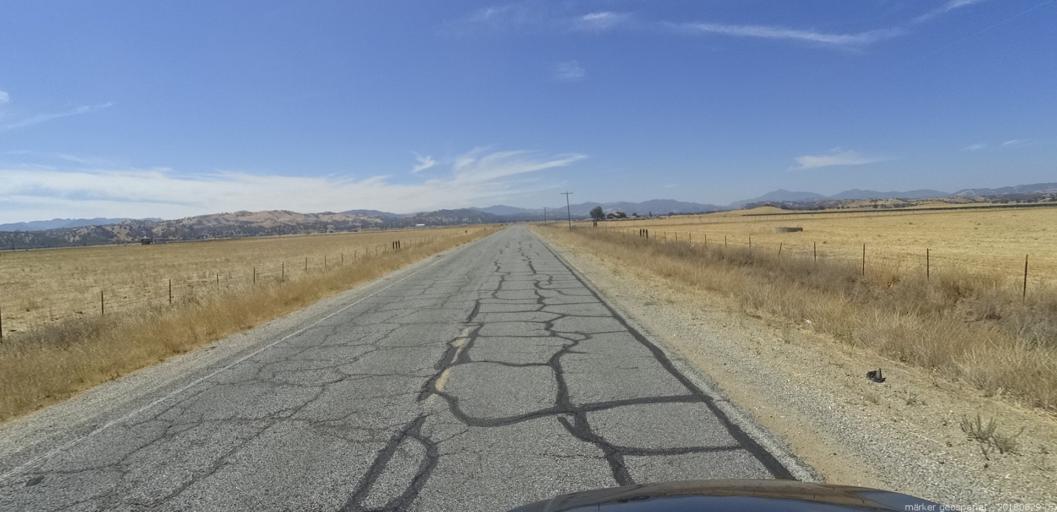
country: US
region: California
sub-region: Monterey County
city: King City
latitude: 35.9410
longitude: -121.1250
